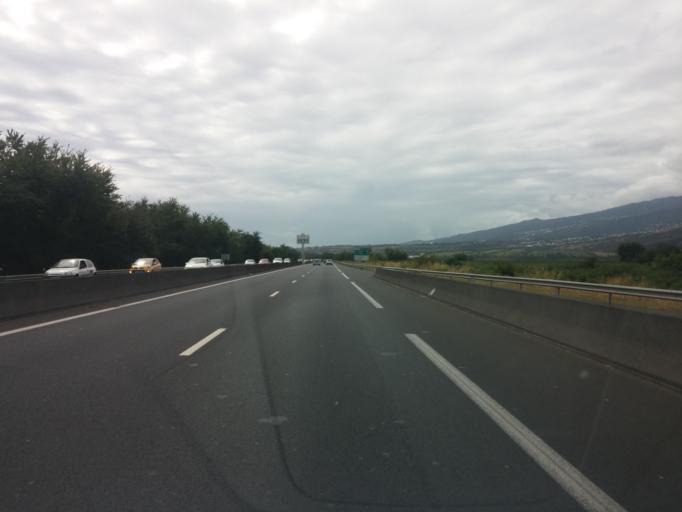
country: RE
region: Reunion
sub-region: Reunion
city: Saint-Paul
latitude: -21.0038
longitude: 55.2815
